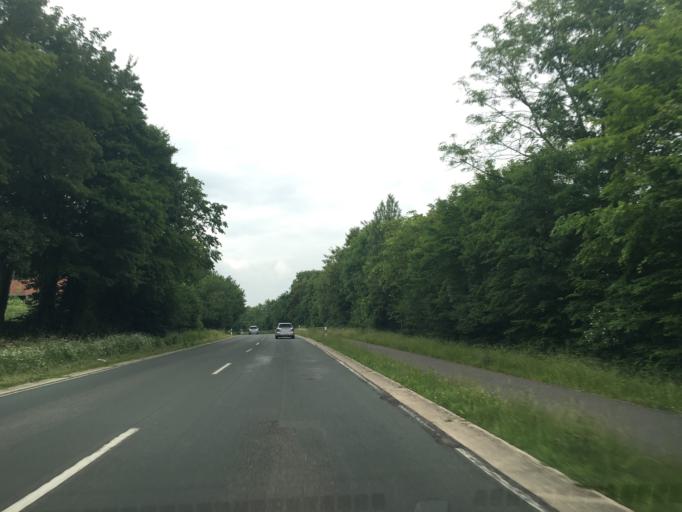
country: DE
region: North Rhine-Westphalia
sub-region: Regierungsbezirk Munster
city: Altenberge
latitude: 52.0496
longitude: 7.4653
